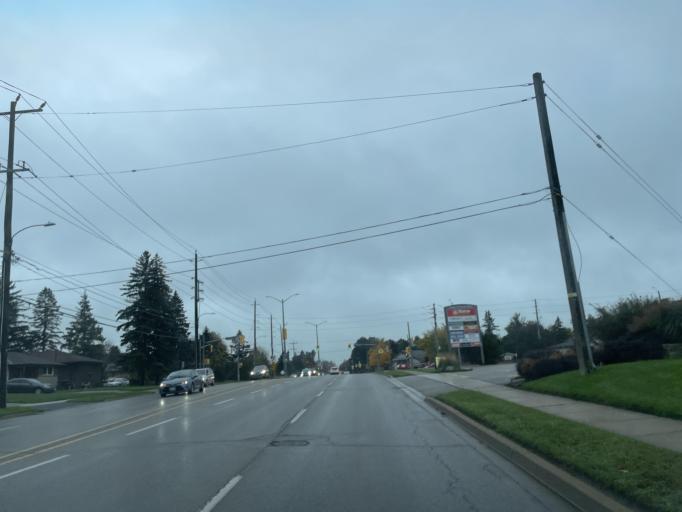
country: CA
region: Ontario
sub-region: Wellington County
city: Guelph
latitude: 43.5574
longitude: -80.2314
